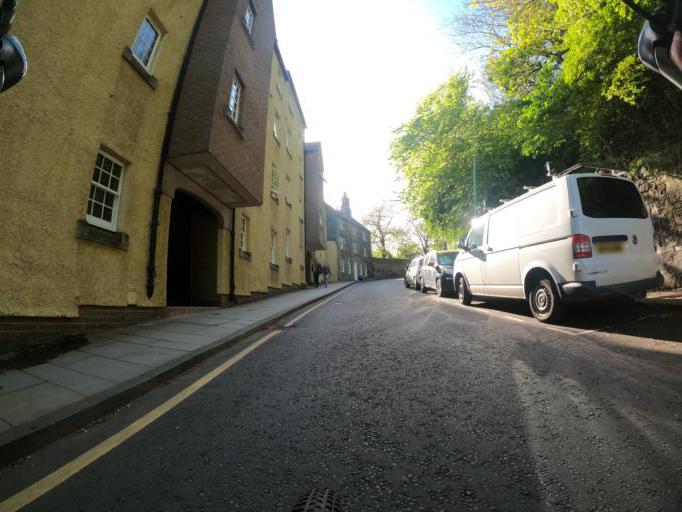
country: GB
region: Scotland
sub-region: Edinburgh
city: Edinburgh
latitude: 55.9527
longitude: -3.2187
